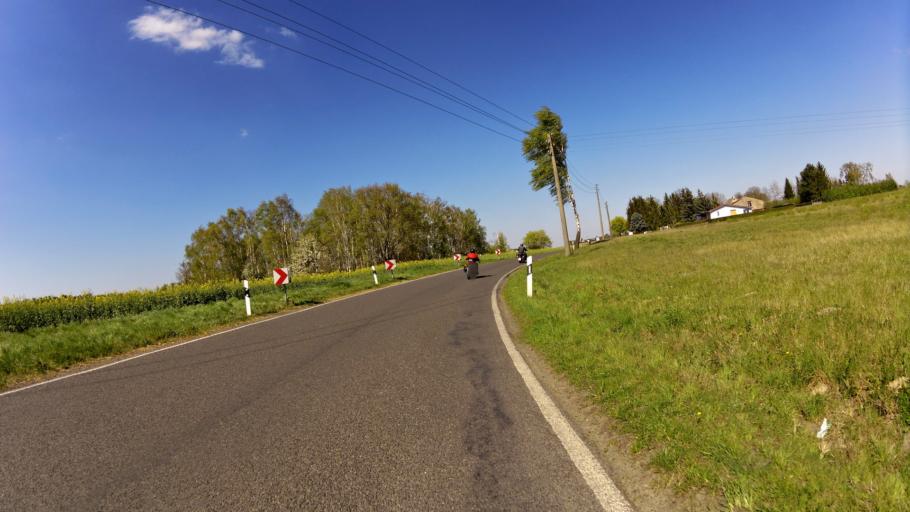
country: DE
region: Brandenburg
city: Muncheberg
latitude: 52.5175
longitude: 14.1488
